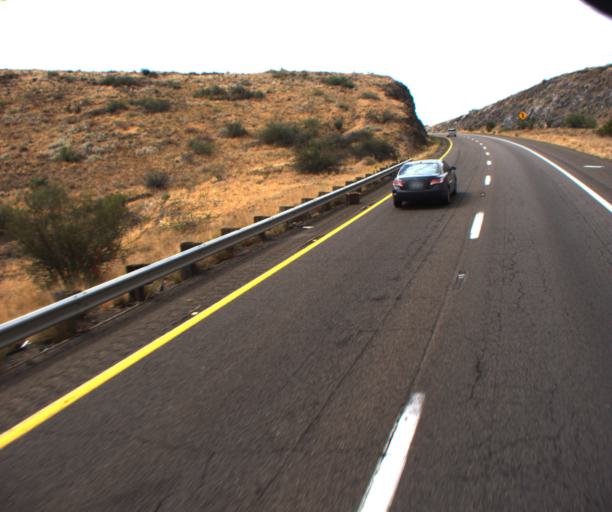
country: US
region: Arizona
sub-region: Yavapai County
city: Cordes Lakes
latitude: 34.2344
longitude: -112.1172
